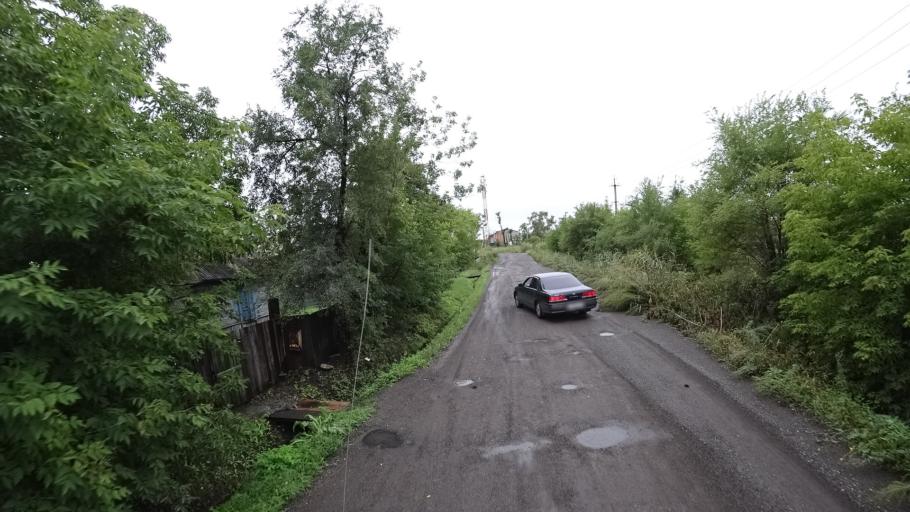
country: RU
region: Primorskiy
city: Monastyrishche
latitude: 44.2095
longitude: 132.4425
